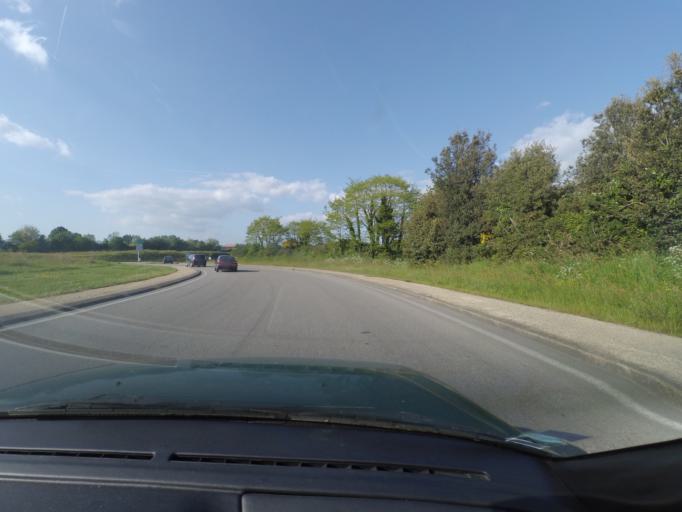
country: FR
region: Pays de la Loire
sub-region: Departement de la Vendee
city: La Roche-sur-Yon
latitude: 46.6651
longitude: -1.4644
